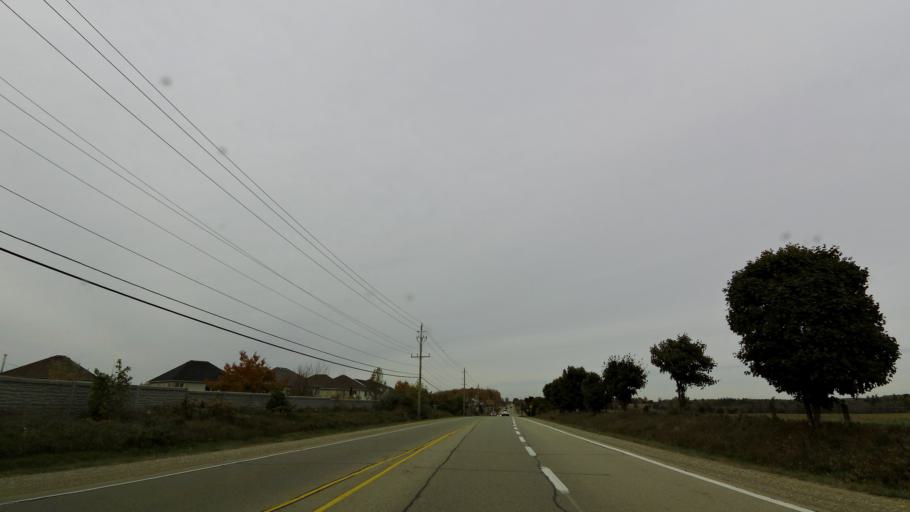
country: CA
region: Ontario
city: Cambridge
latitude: 43.4263
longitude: -80.2853
